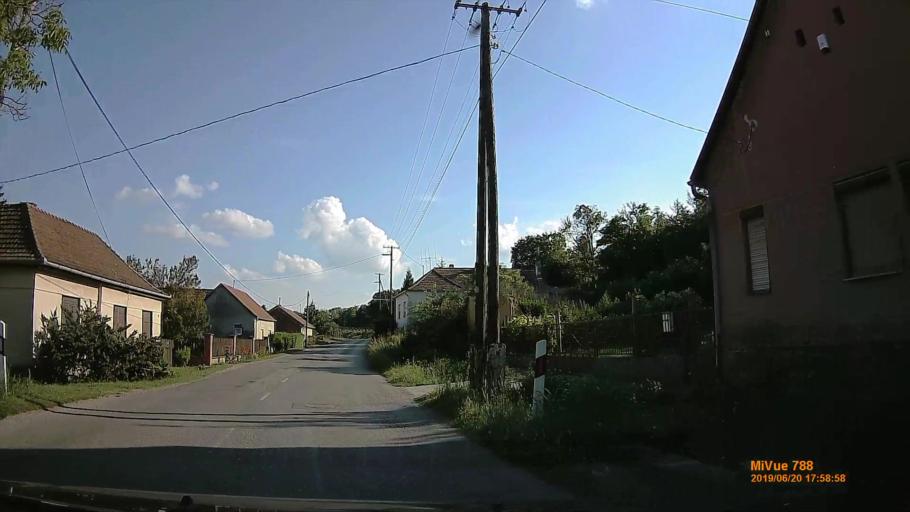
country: HU
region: Baranya
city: Buekkoesd
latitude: 46.1009
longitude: 17.9879
